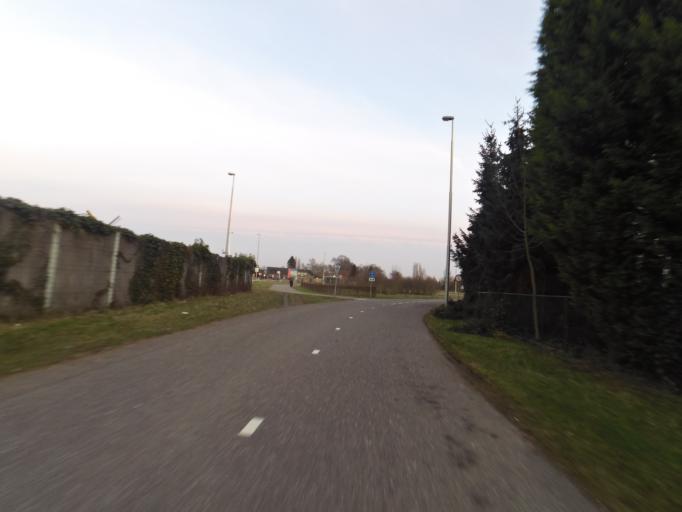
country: NL
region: Gelderland
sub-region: Gemeente Zevenaar
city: Zevenaar
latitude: 51.9154
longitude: 6.0924
